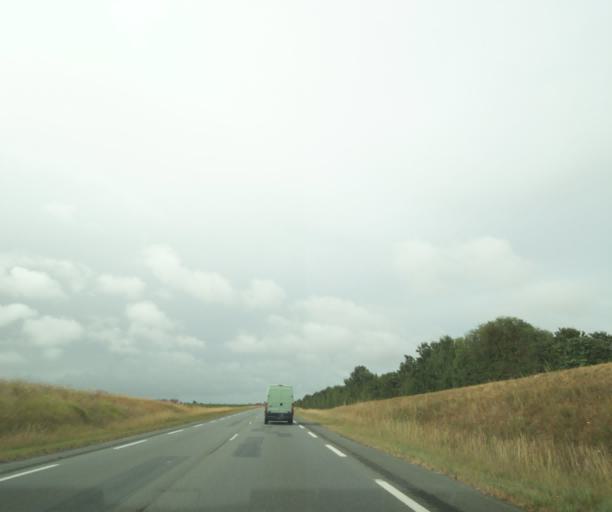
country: FR
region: Poitou-Charentes
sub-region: Departement de la Charente-Maritime
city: Lagord
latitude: 46.1996
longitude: -1.1392
